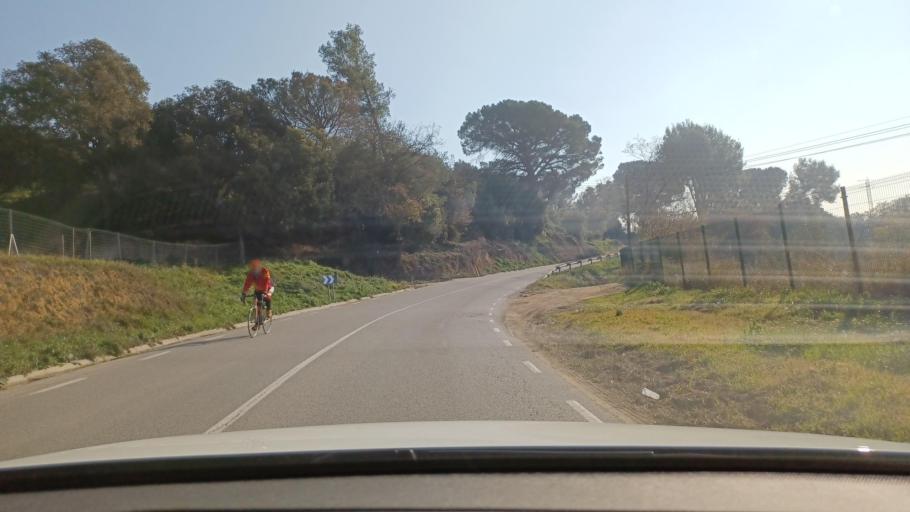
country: ES
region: Catalonia
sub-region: Provincia de Barcelona
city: Santa Eulalia de Roncana
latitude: 41.6659
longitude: 2.2341
